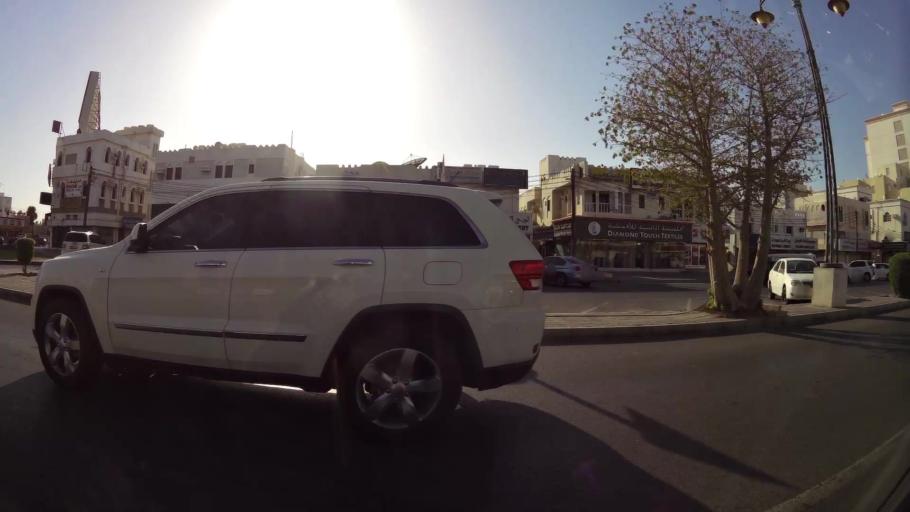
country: OM
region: Muhafazat Masqat
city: As Sib al Jadidah
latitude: 23.6304
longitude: 58.1972
